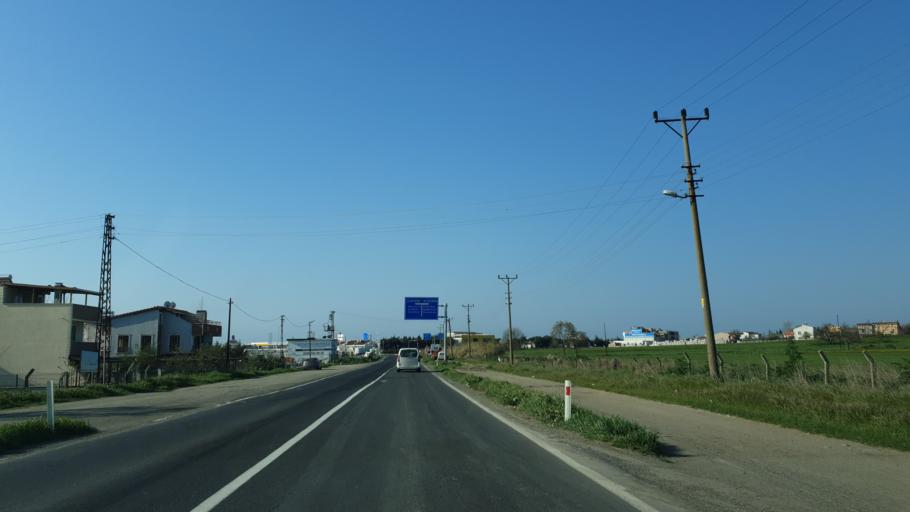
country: TR
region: Tekirdag
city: Corlu
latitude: 41.0128
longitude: 27.7181
